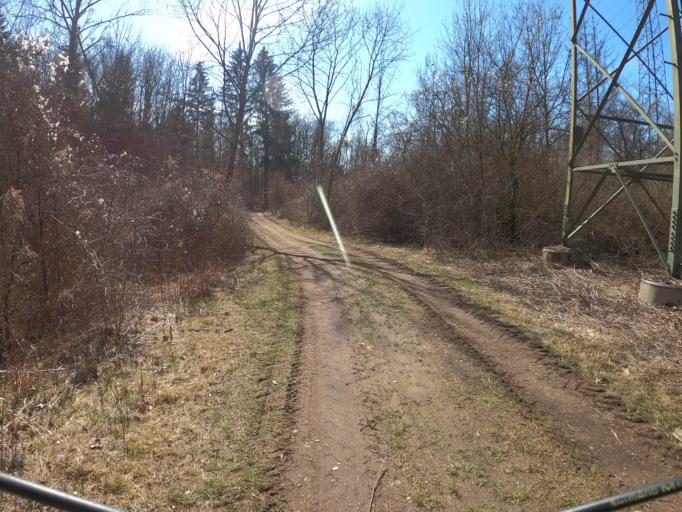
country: DE
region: Bavaria
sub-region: Swabia
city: Nersingen
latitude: 48.4416
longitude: 10.1347
